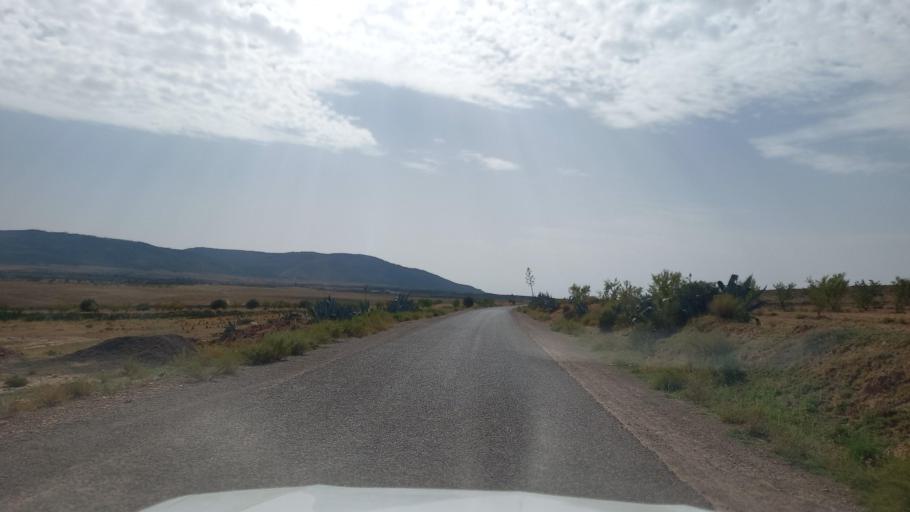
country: TN
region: Al Qasrayn
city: Kasserine
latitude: 35.3615
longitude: 8.8448
